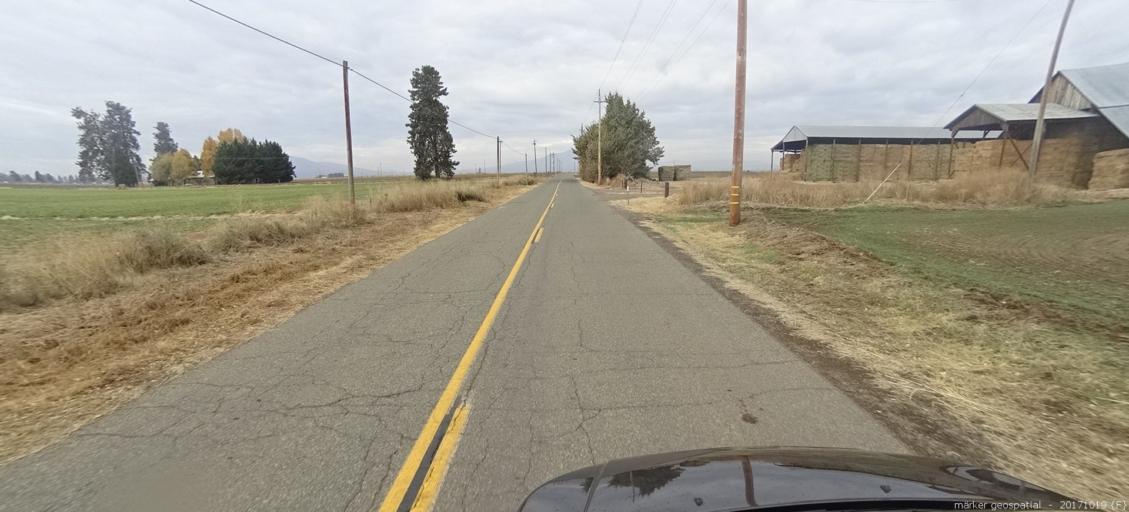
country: US
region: California
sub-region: Shasta County
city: Burney
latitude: 41.0769
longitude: -121.3585
